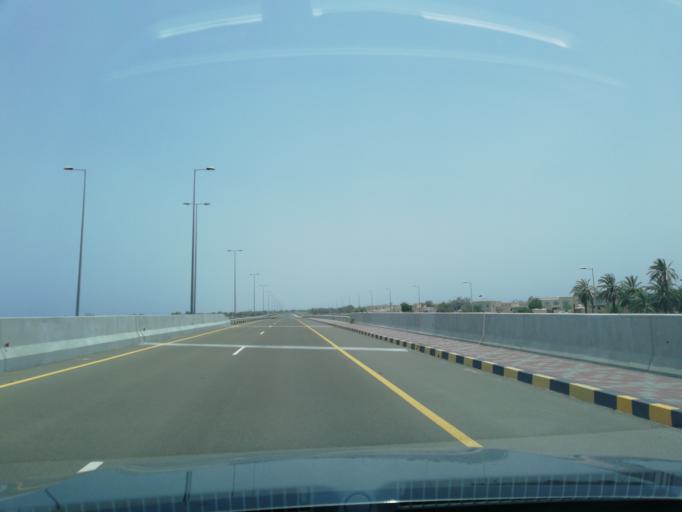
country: OM
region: Al Batinah
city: Shinas
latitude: 24.7672
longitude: 56.4601
